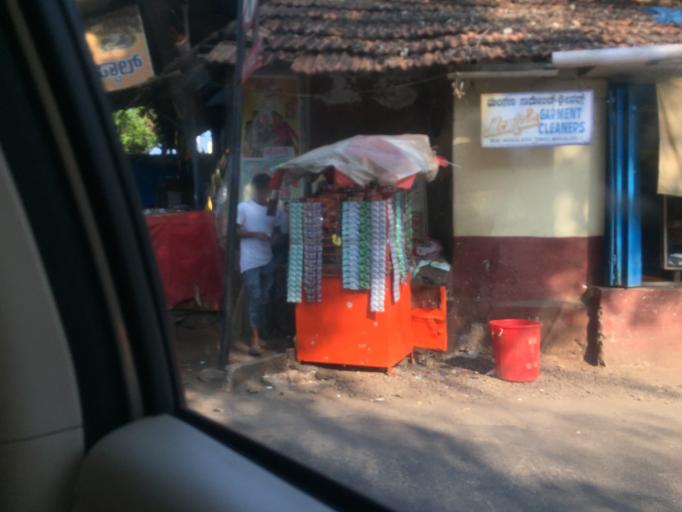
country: IN
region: Karnataka
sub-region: Dakshina Kannada
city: Ullal
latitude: 12.8490
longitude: 74.8459
